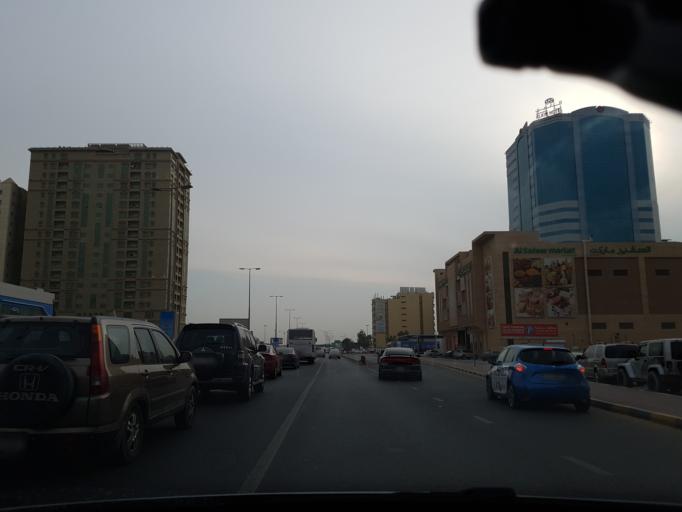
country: AE
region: Ajman
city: Ajman
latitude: 25.3781
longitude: 55.4595
